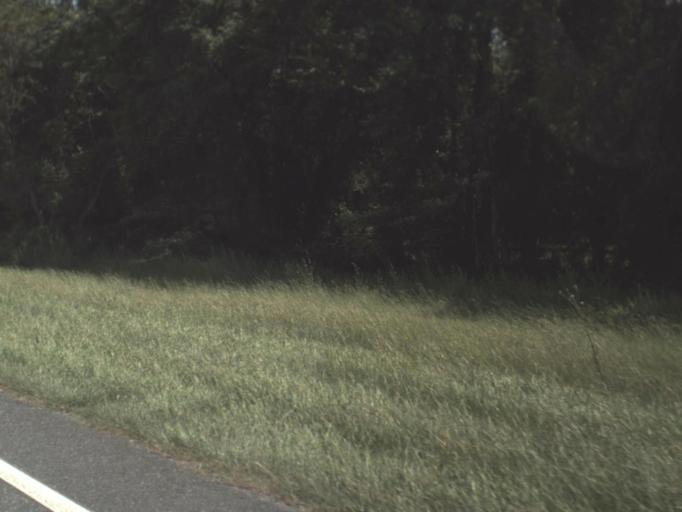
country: US
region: Florida
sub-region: Columbia County
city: Watertown
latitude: 30.1165
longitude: -82.6160
